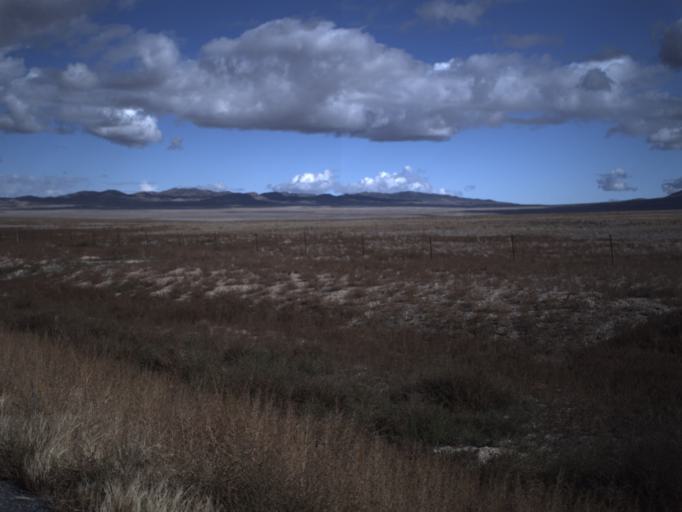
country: US
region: Utah
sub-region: Beaver County
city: Milford
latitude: 38.6347
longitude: -113.8569
